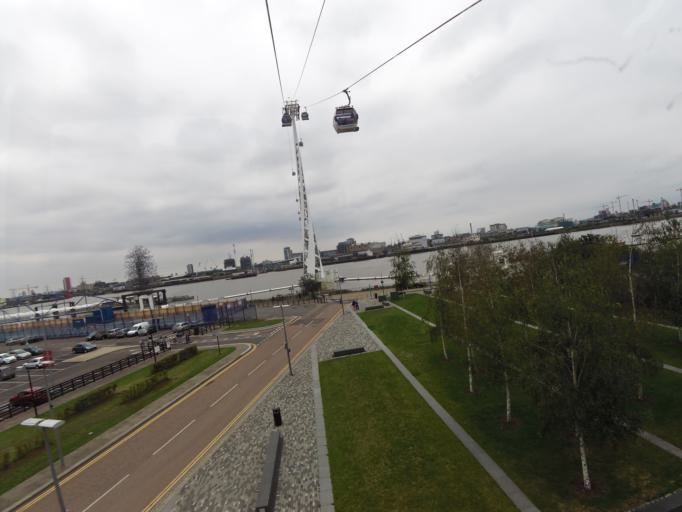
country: GB
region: England
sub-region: Greater London
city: Poplar
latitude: 51.4999
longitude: 0.0084
